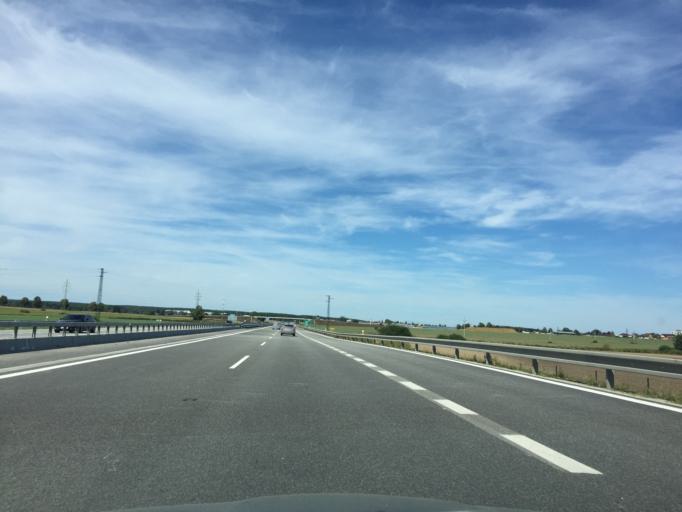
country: CZ
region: Jihocesky
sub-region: Okres Tabor
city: Veseli nad Luznici
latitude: 49.1772
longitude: 14.6793
